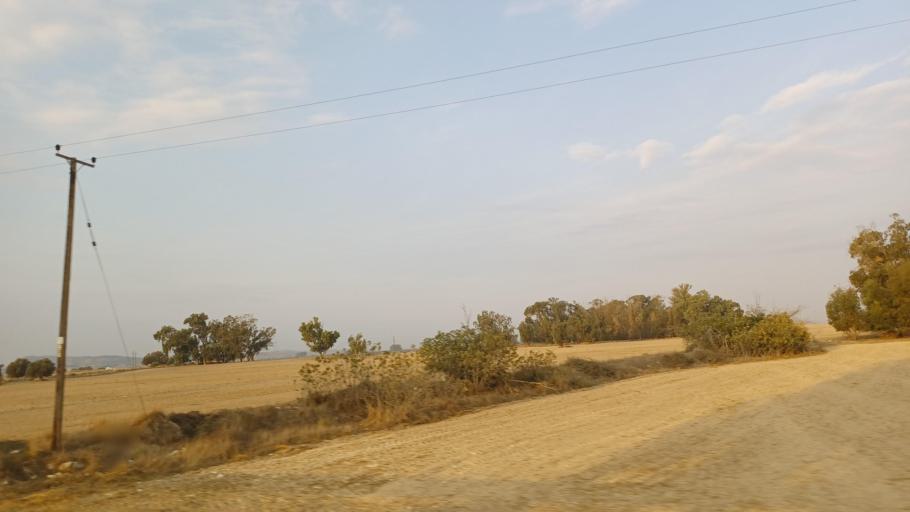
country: CY
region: Lefkosia
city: Lympia
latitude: 35.0348
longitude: 33.4929
